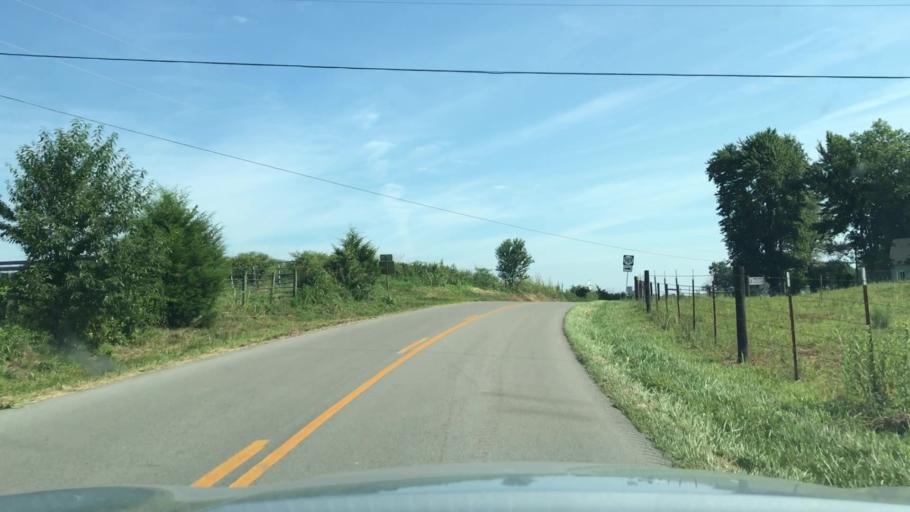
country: US
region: Tennessee
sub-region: Pickett County
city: Byrdstown
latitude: 36.6343
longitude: -85.0857
